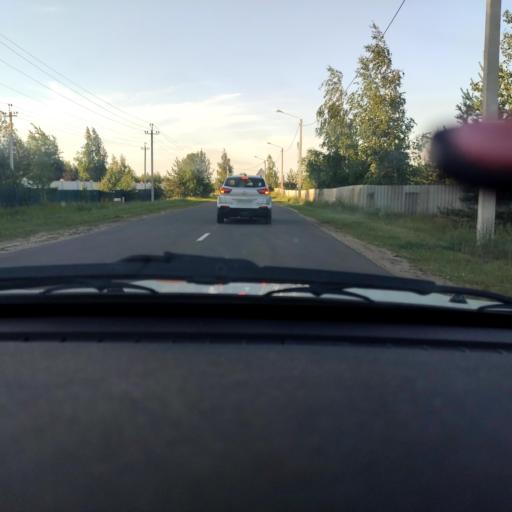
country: RU
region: Voronezj
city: Ramon'
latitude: 51.8905
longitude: 39.2529
